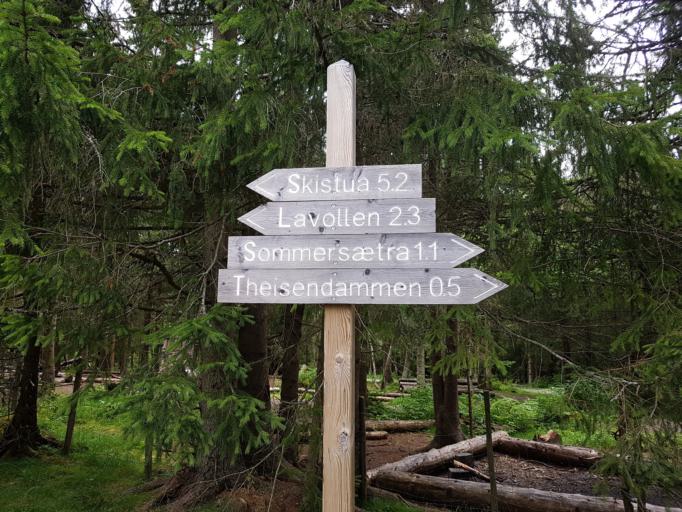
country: NO
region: Sor-Trondelag
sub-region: Trondheim
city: Trondheim
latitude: 63.4184
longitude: 10.3404
